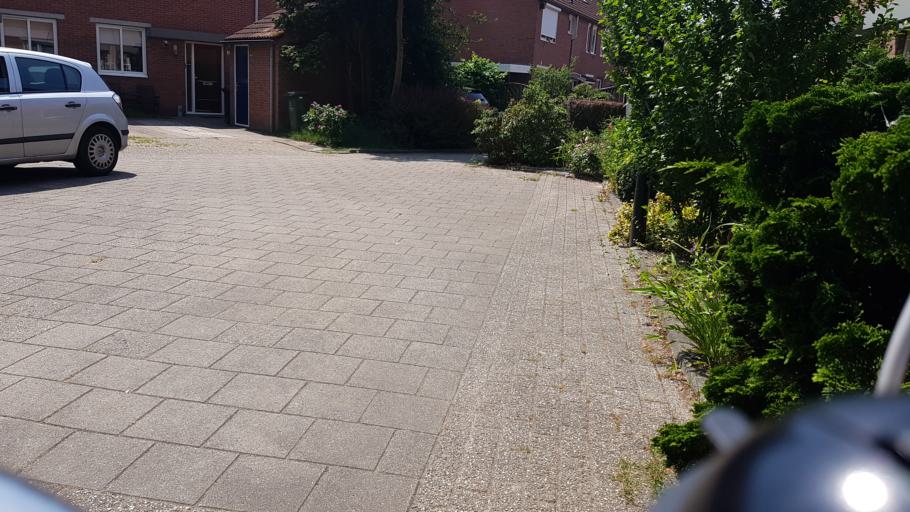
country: NL
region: Gelderland
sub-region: Gemeente Apeldoorn
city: Apeldoorn
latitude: 52.1919
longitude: 6.0011
